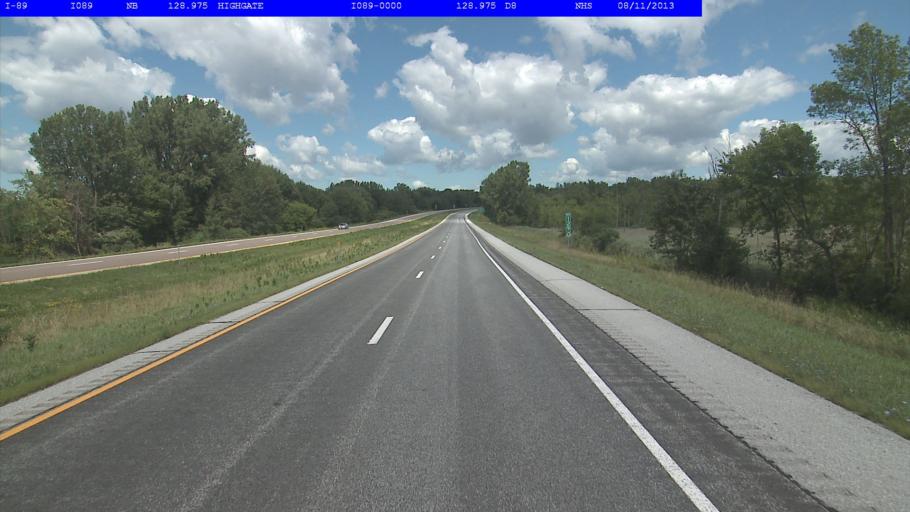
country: US
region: Vermont
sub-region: Franklin County
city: Swanton
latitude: 44.9971
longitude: -73.0860
